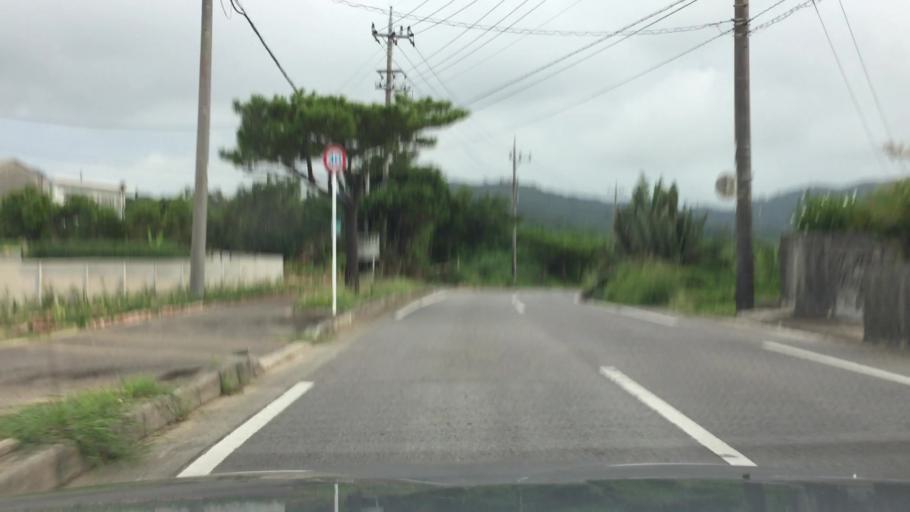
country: JP
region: Okinawa
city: Ishigaki
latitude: 24.3908
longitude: 124.1551
